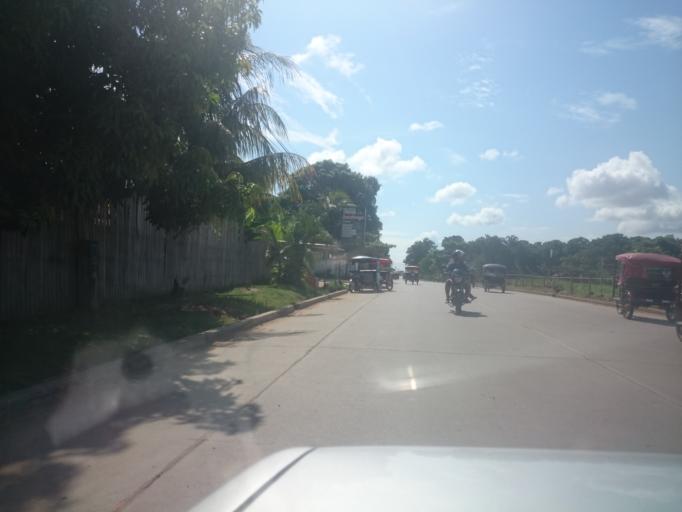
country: PE
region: Ucayali
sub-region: Provincia de Coronel Portillo
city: Puerto Callao
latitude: -8.3635
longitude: -74.5690
